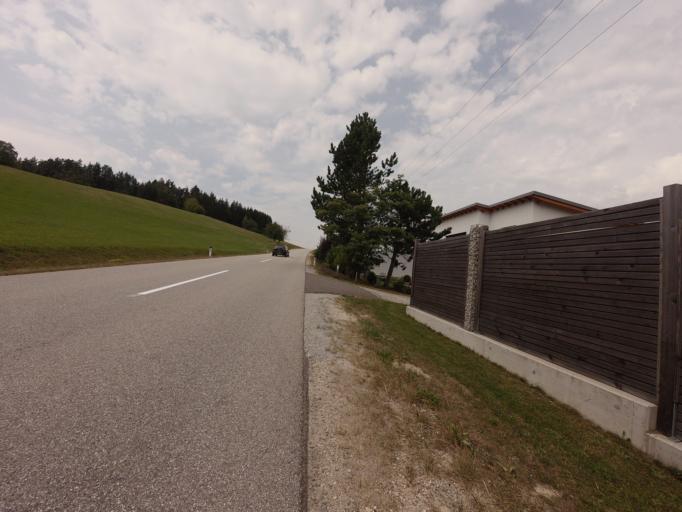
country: AT
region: Upper Austria
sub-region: Politischer Bezirk Urfahr-Umgebung
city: Reichenthal
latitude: 48.5555
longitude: 14.4146
